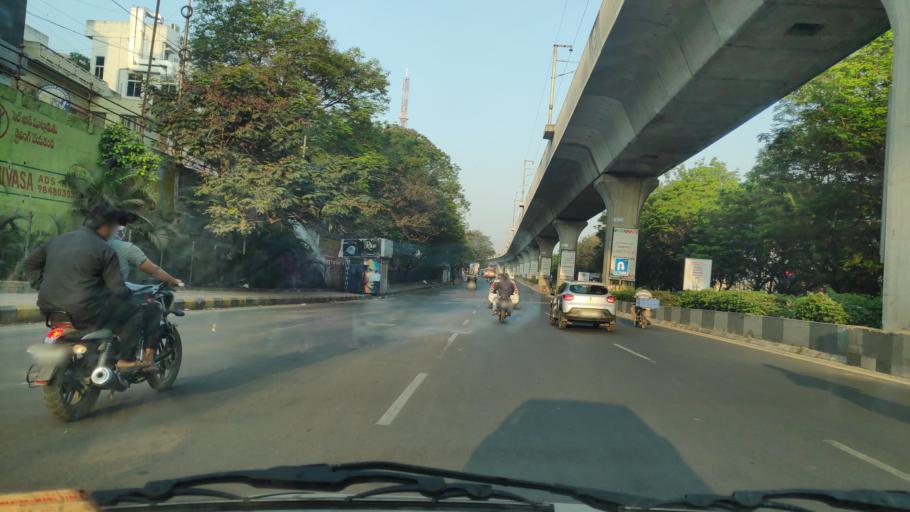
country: IN
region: Telangana
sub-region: Rangareddi
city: Gaddi Annaram
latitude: 17.3691
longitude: 78.5180
